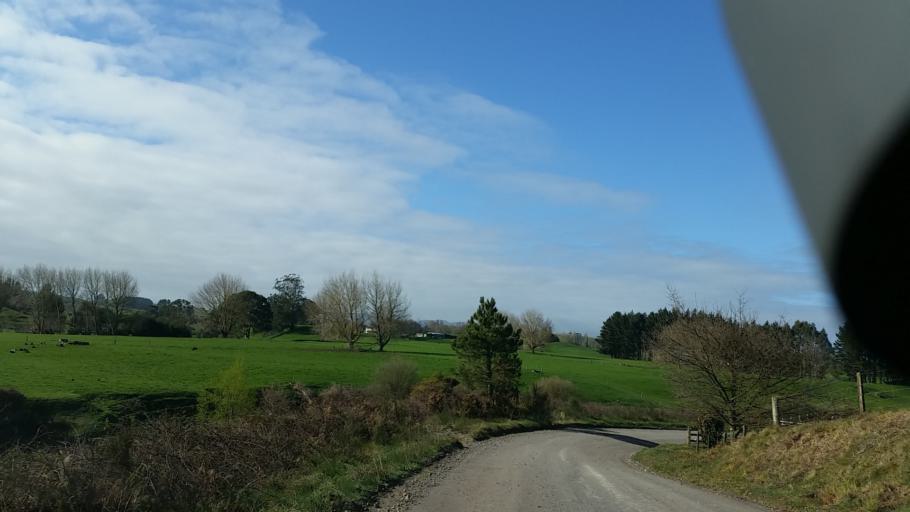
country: NZ
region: Bay of Plenty
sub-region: Rotorua District
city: Rotorua
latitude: -38.2619
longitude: 176.1597
